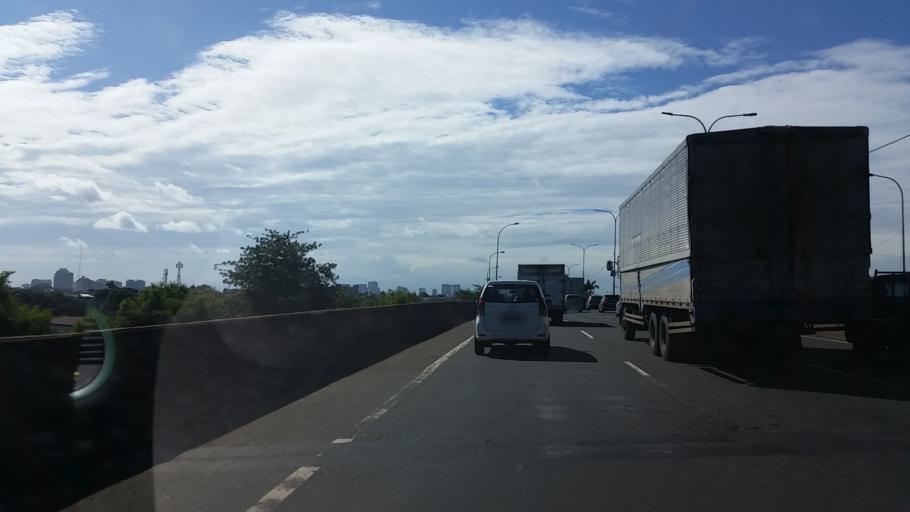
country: ID
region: Banten
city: South Tangerang
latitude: -6.2549
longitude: 106.7649
